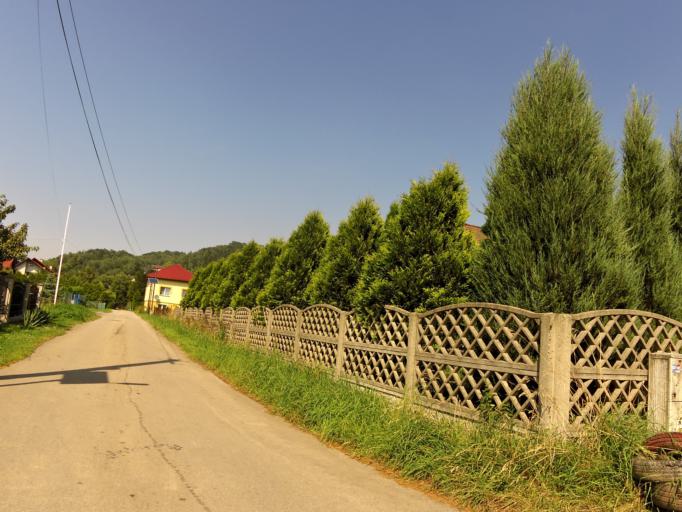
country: PL
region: Silesian Voivodeship
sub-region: Powiat zywiecki
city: Wieprz
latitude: 49.6517
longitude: 19.1812
